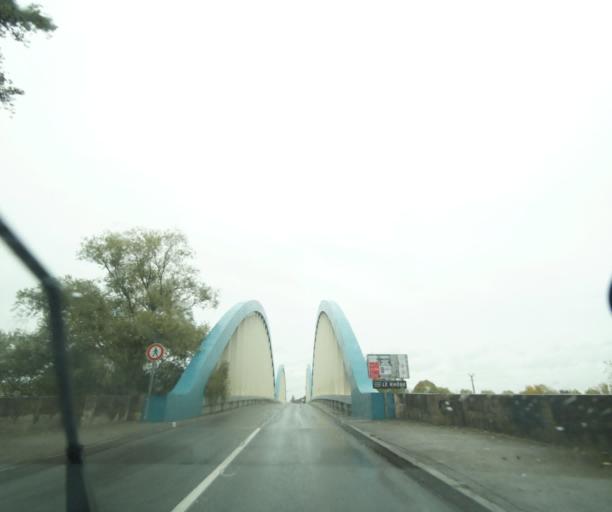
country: FR
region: Rhone-Alpes
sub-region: Departement de l'Ain
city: Loyettes
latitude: 45.7713
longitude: 5.2057
